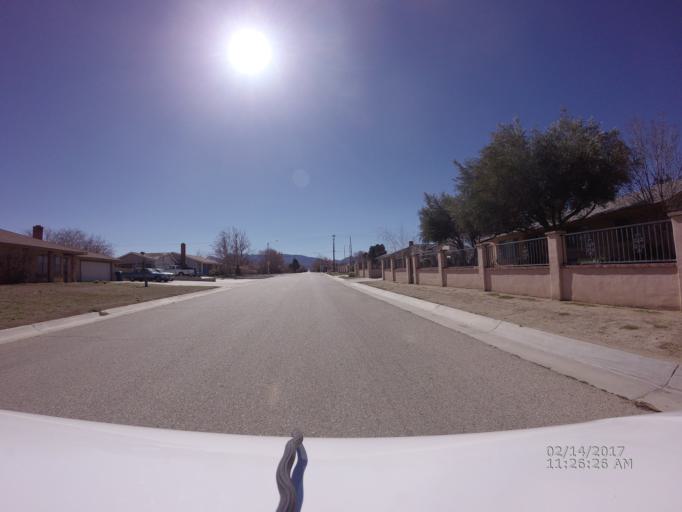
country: US
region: California
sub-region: Los Angeles County
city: Littlerock
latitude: 34.5587
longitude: -117.9582
